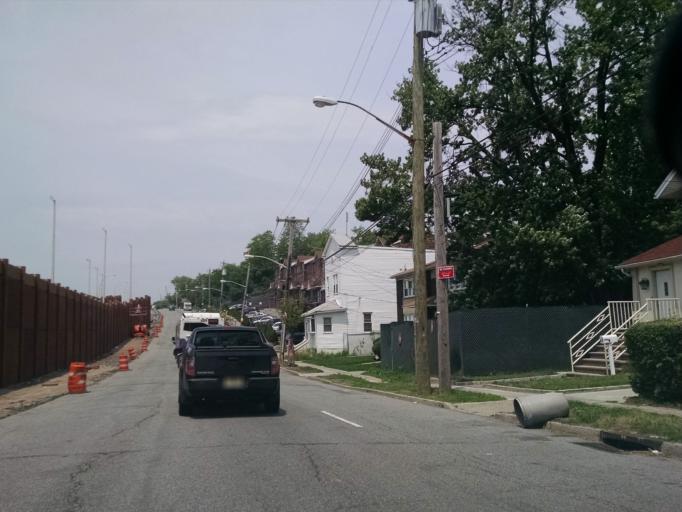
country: US
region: New York
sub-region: Kings County
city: Bensonhurst
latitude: 40.6048
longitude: -74.0701
